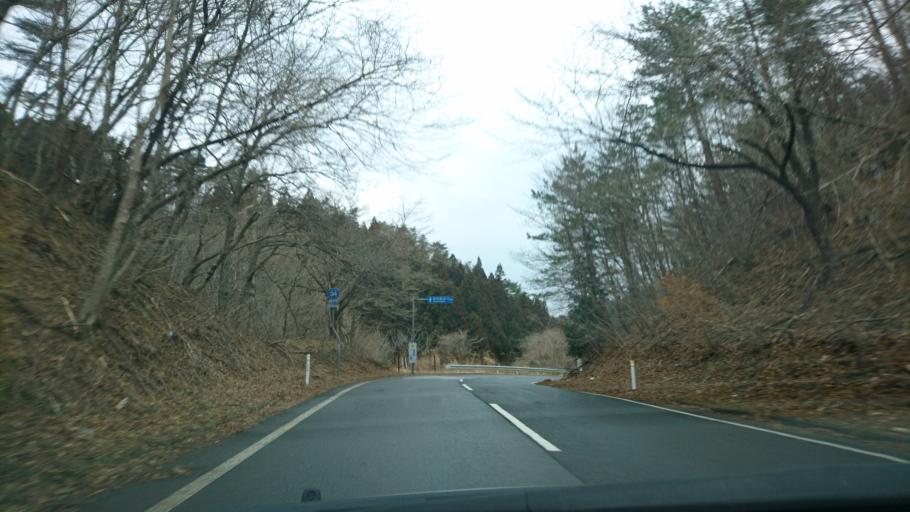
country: JP
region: Iwate
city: Ofunato
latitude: 38.9961
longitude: 141.5470
